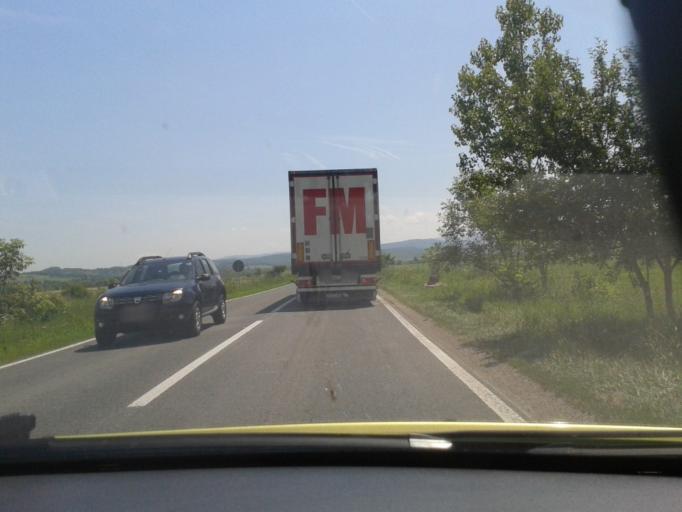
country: RO
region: Timis
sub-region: Comuna Margina
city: Margina
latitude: 45.8562
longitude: 22.2753
